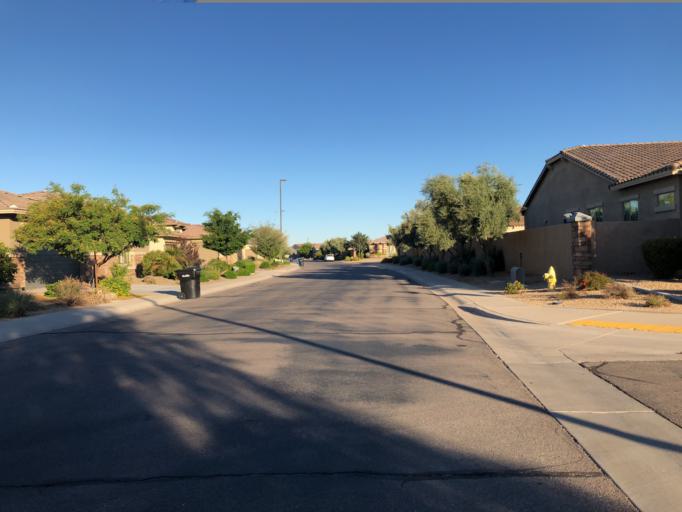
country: US
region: Arizona
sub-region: Maricopa County
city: Queen Creek
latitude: 33.2276
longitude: -111.7091
